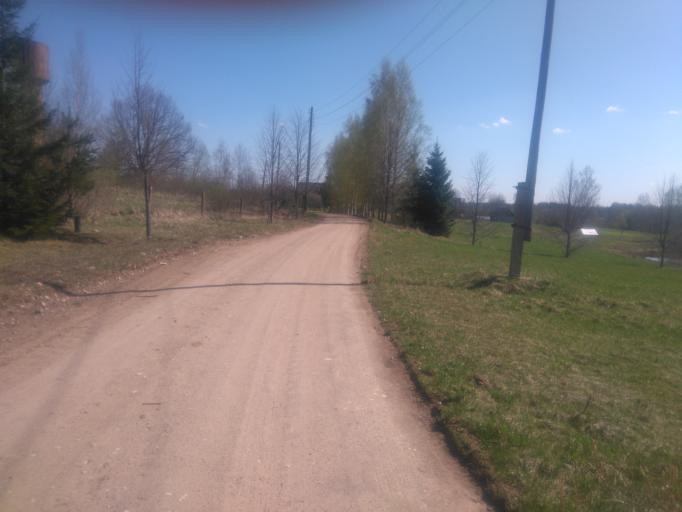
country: LV
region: Vecpiebalga
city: Vecpiebalga
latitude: 57.0270
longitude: 25.8455
